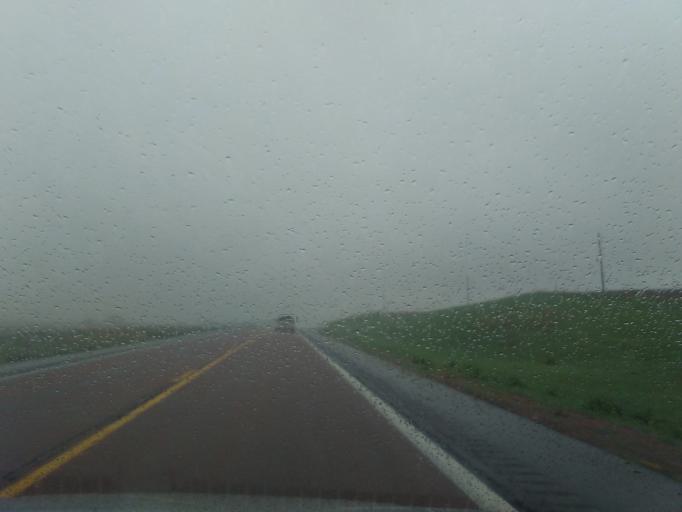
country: US
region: Nebraska
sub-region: Wayne County
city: Wayne
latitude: 42.2356
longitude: -97.1209
